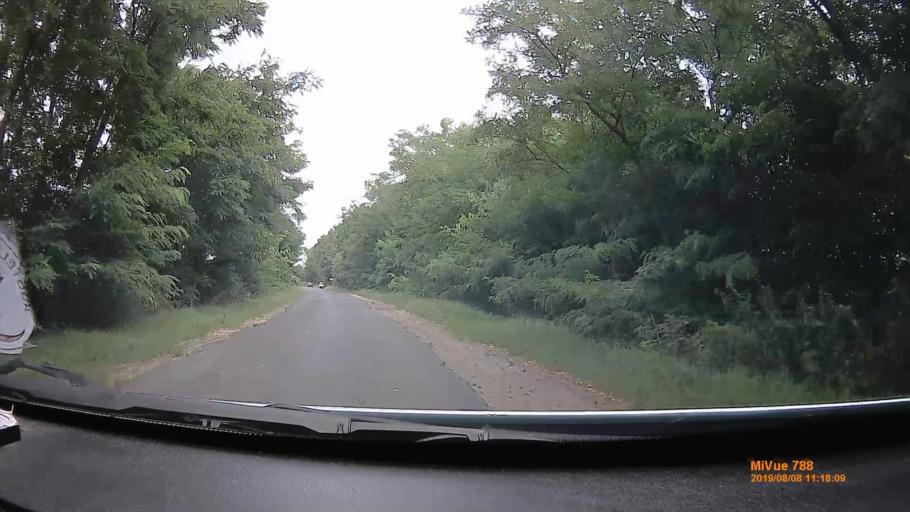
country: HU
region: Szabolcs-Szatmar-Bereg
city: Balkany
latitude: 47.7353
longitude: 21.8363
